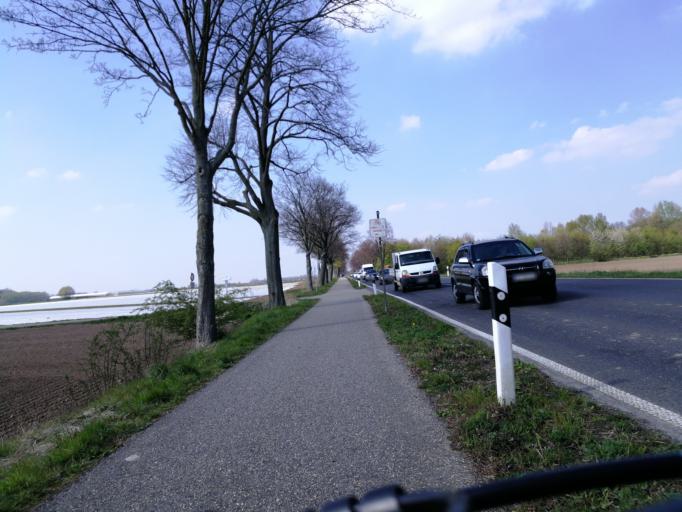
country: DE
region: North Rhine-Westphalia
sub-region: Regierungsbezirk Dusseldorf
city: Dormagen
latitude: 51.1227
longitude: 6.7646
